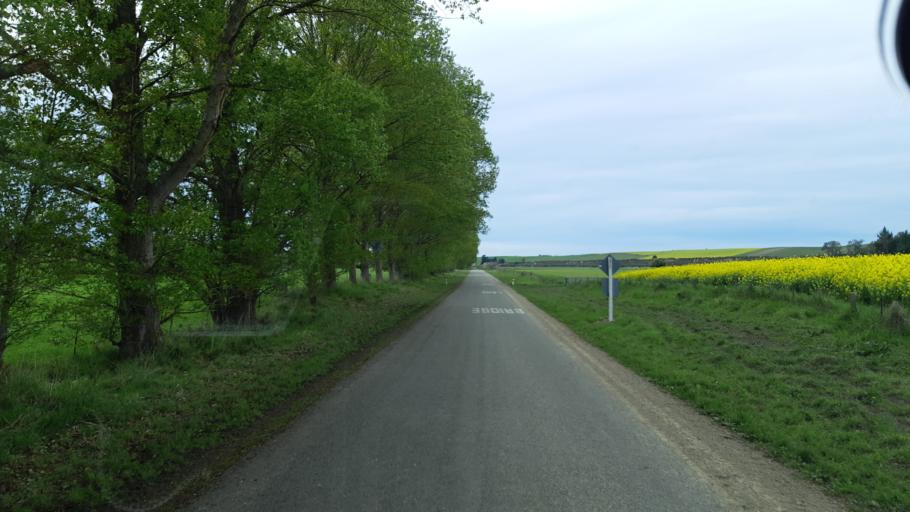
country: NZ
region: Canterbury
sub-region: Timaru District
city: Timaru
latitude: -44.5332
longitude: 171.1183
